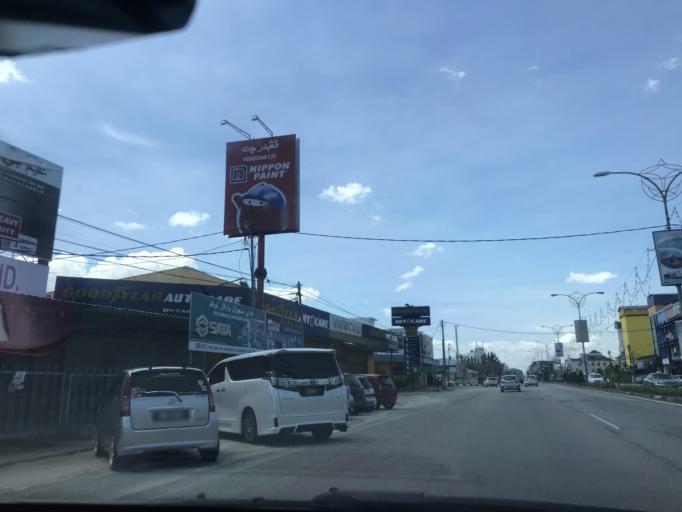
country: MY
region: Kelantan
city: Kota Bharu
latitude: 6.1075
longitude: 102.2574
